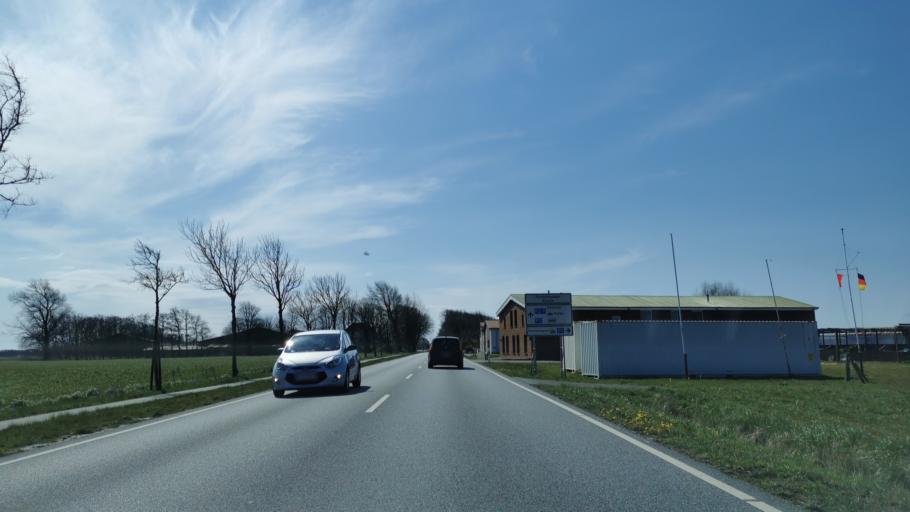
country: DE
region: Schleswig-Holstein
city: Oesterdeichstrich
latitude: 54.1505
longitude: 8.8779
